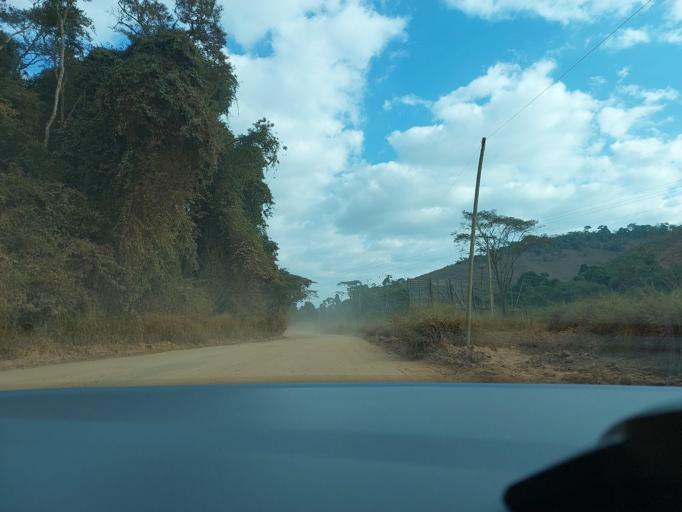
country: BR
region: Minas Gerais
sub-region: Visconde Do Rio Branco
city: Visconde do Rio Branco
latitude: -20.8535
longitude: -42.6667
